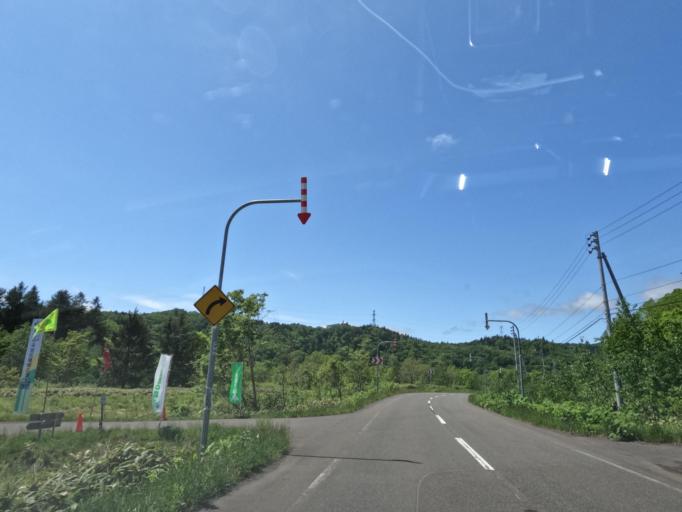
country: JP
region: Hokkaido
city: Tobetsu
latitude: 43.4185
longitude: 141.5814
